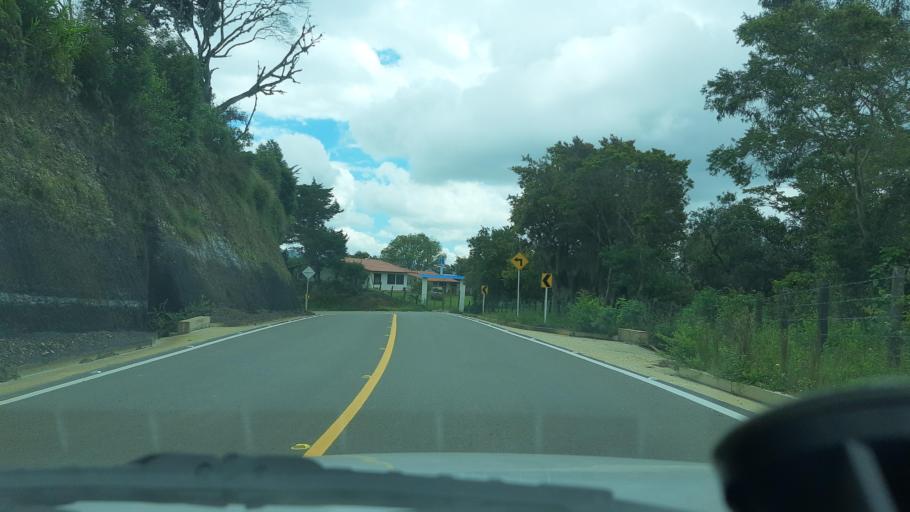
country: CO
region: Boyaca
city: Moniquira
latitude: 5.8076
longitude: -73.5967
